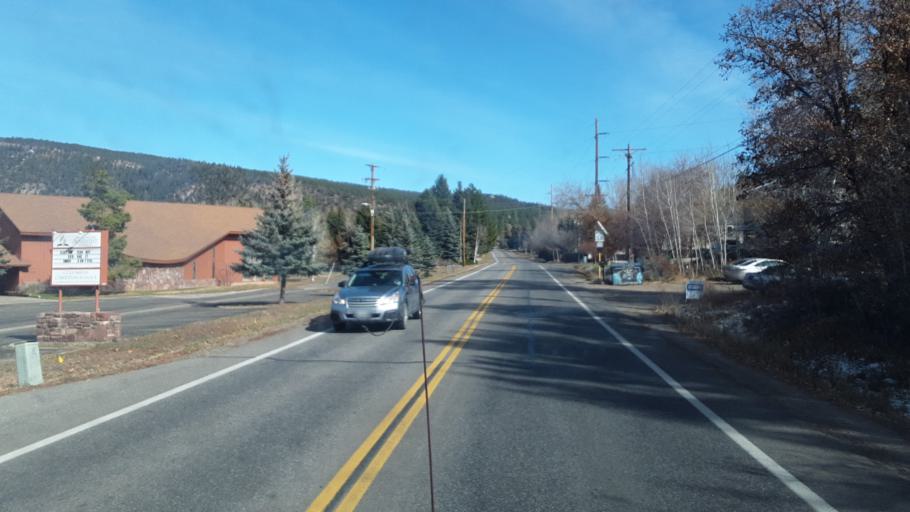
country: US
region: Colorado
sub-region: La Plata County
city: Durango
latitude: 37.3007
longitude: -107.8414
